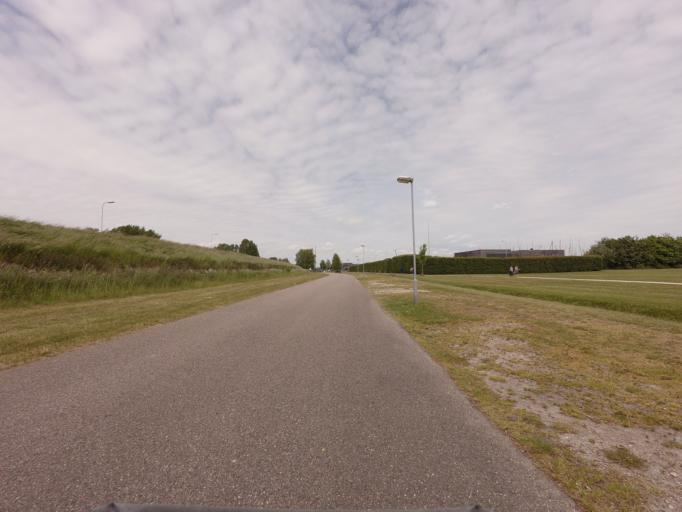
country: NL
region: North Holland
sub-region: Gemeente Medemblik
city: Medemblik
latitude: 52.7670
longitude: 5.1172
